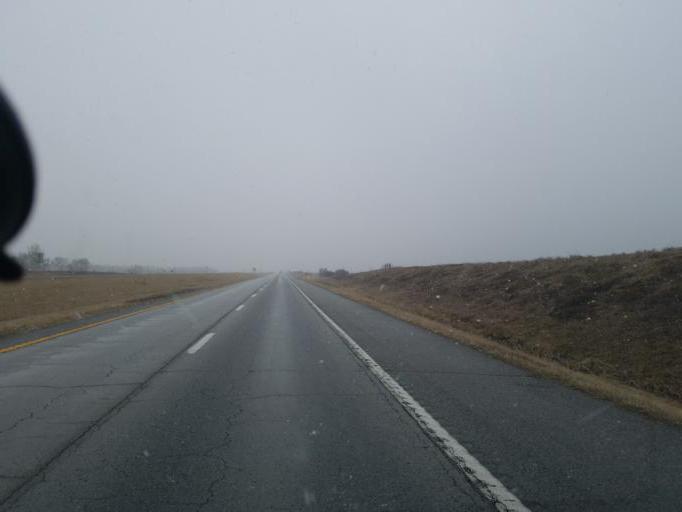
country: US
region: Missouri
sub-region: Macon County
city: La Plata
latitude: 39.9542
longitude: -92.4769
